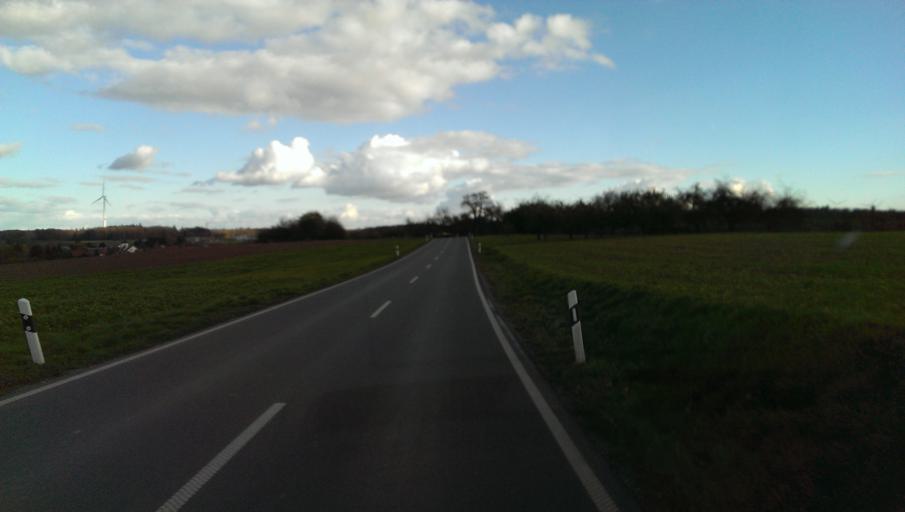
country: DE
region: Baden-Wuerttemberg
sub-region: Regierungsbezirk Stuttgart
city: Buch am Ahorn
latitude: 49.5381
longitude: 9.5455
